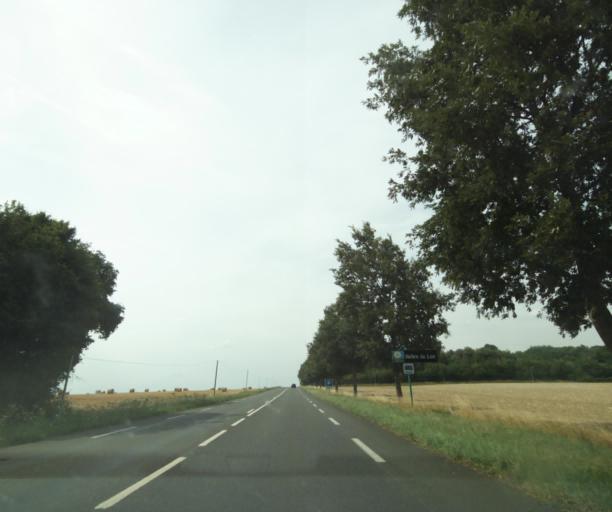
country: FR
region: Centre
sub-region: Departement d'Indre-et-Loire
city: Saint-Christophe-sur-le-Nais
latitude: 47.6507
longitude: 0.4929
